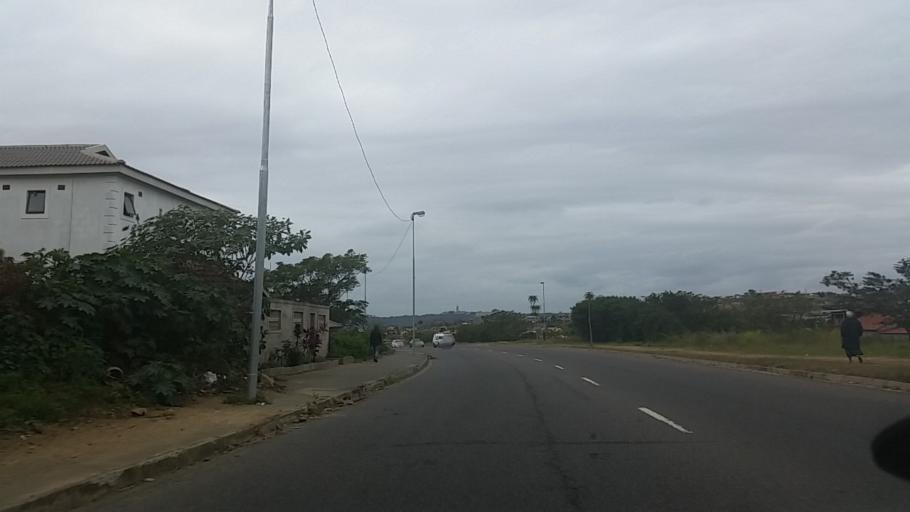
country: ZA
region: KwaZulu-Natal
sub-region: eThekwini Metropolitan Municipality
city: Berea
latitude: -29.8585
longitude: 30.9423
